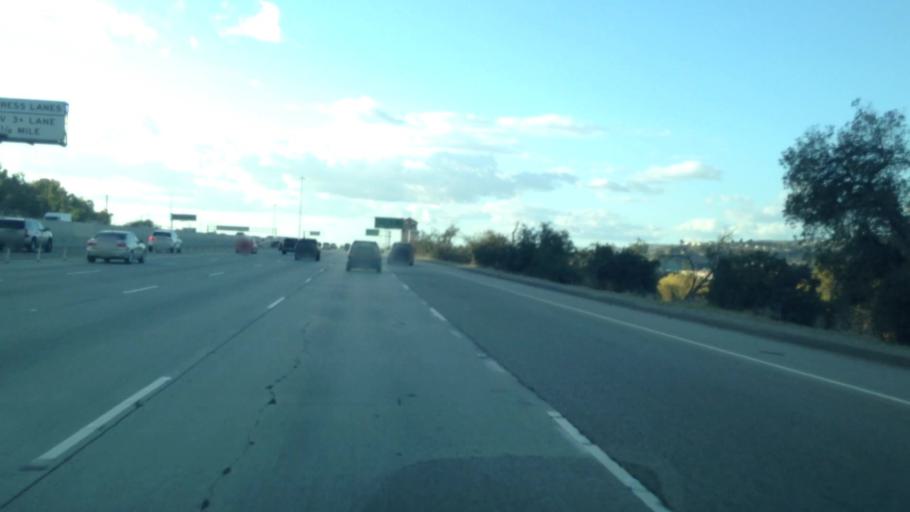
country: US
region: California
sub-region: Orange County
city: Yorba Linda
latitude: 33.8690
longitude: -117.7294
